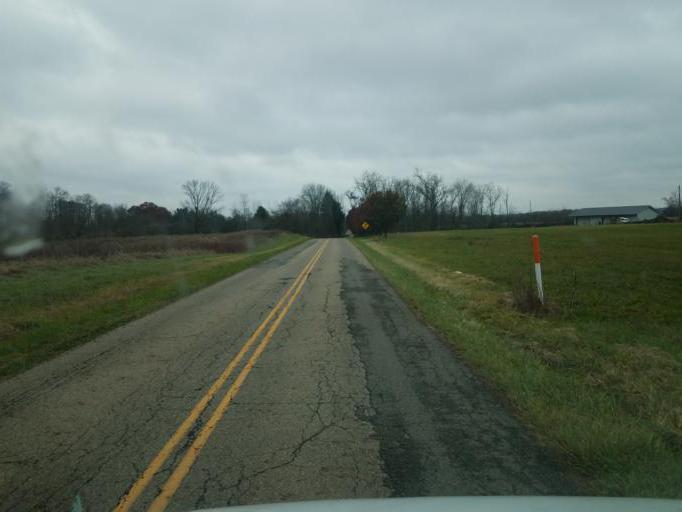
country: US
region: Ohio
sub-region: Knox County
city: Centerburg
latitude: 40.3612
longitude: -82.6234
